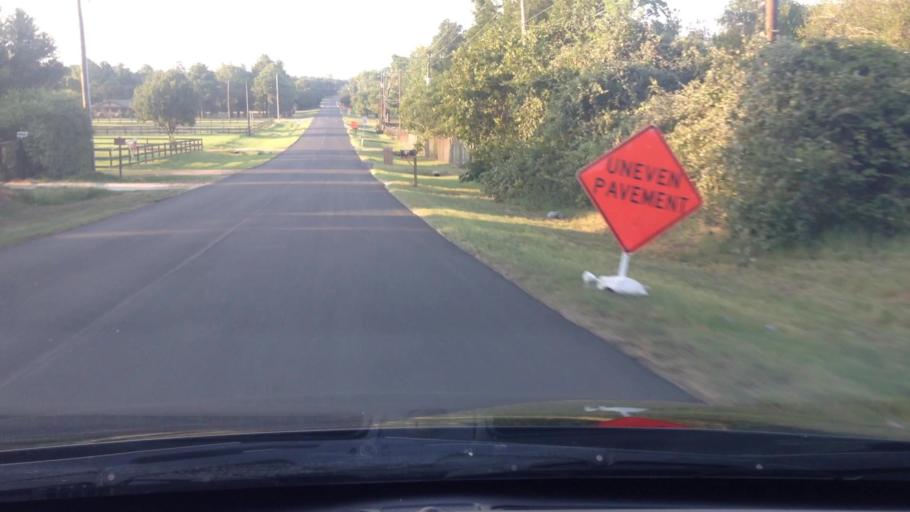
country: US
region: Texas
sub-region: Tarrant County
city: Rendon
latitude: 32.5965
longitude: -97.2502
